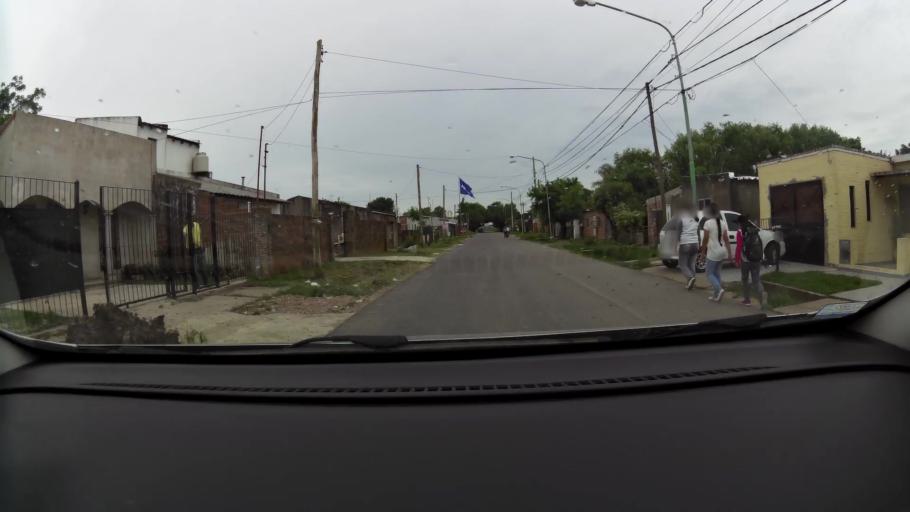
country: AR
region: Buenos Aires
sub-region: Partido de Campana
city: Campana
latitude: -34.2086
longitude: -58.9346
